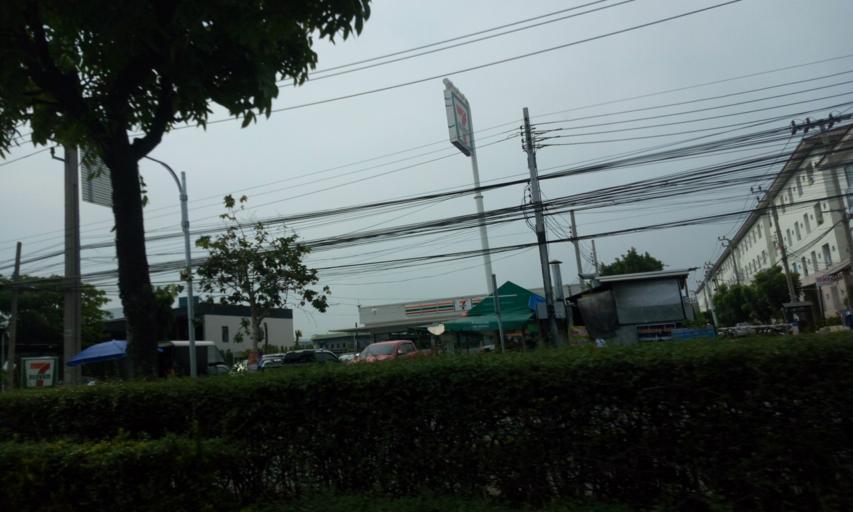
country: TH
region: Bangkok
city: Lat Krabang
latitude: 13.7217
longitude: 100.7648
